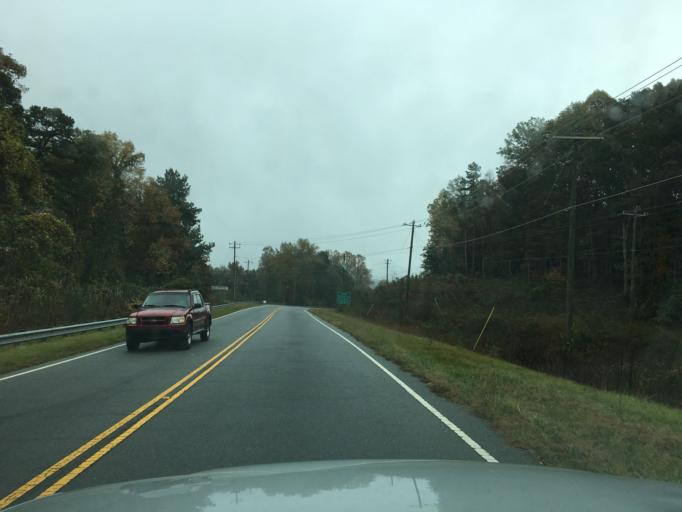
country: US
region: South Carolina
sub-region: Oconee County
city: Utica
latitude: 34.7861
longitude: -82.9002
